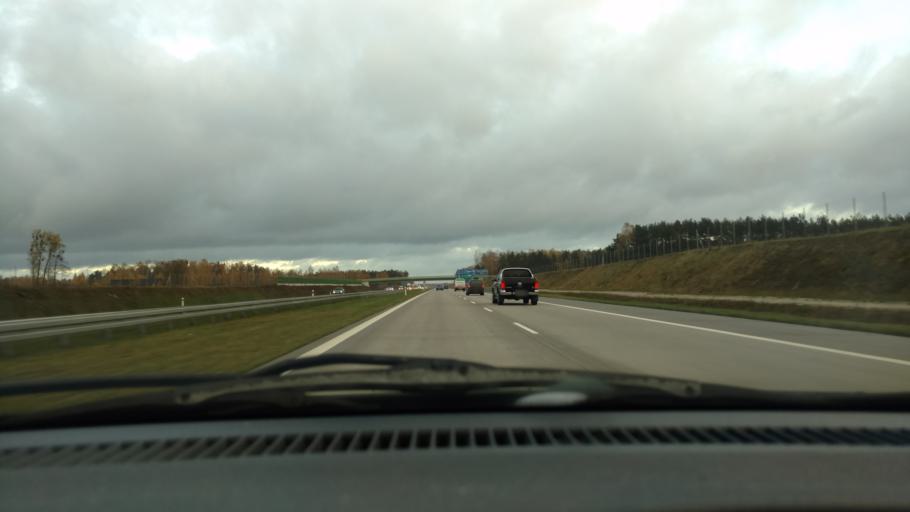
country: PL
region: Lodz Voivodeship
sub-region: Powiat lodzki wschodni
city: Brojce
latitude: 51.6573
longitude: 19.5807
